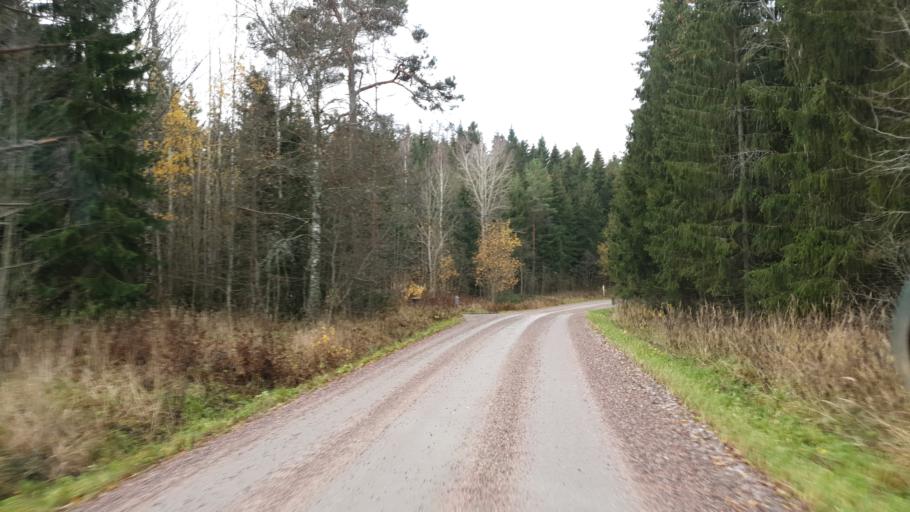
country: FI
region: Uusimaa
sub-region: Helsinki
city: Siuntio
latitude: 60.1464
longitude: 24.2695
